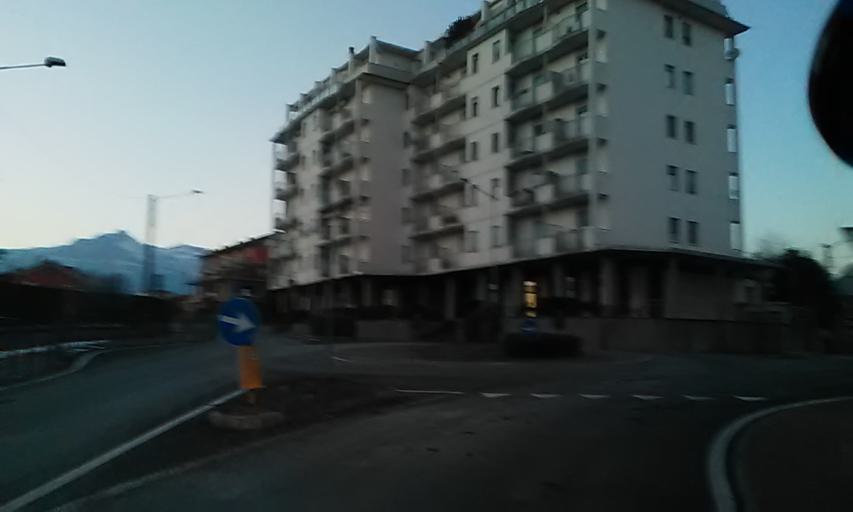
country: IT
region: Piedmont
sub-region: Provincia di Biella
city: Vigliano Biellese
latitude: 45.5582
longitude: 8.0958
